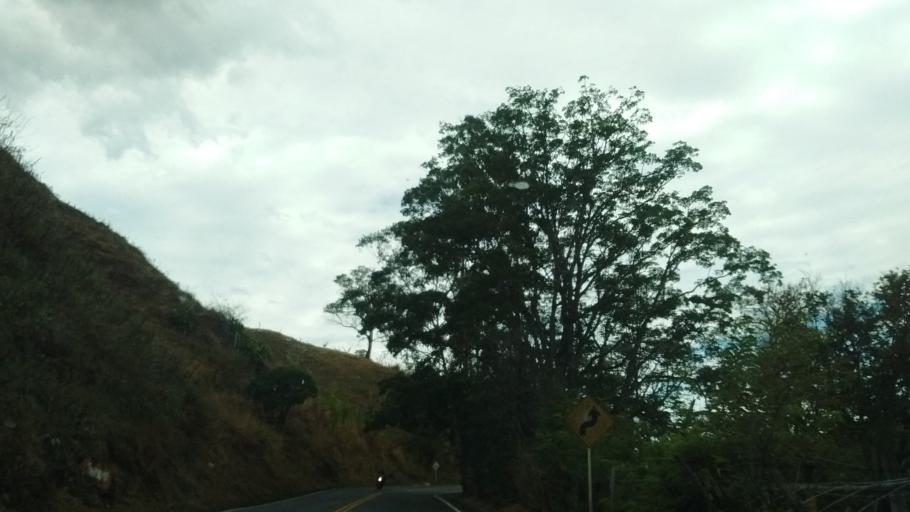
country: CO
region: Cauca
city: Rosas
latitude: 2.2807
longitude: -76.7145
